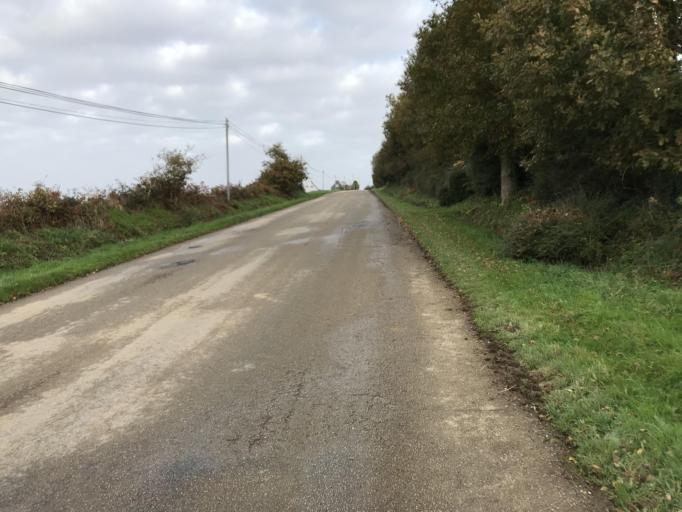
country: FR
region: Brittany
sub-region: Departement du Finistere
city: Irvillac
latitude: 48.3566
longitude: -4.2156
